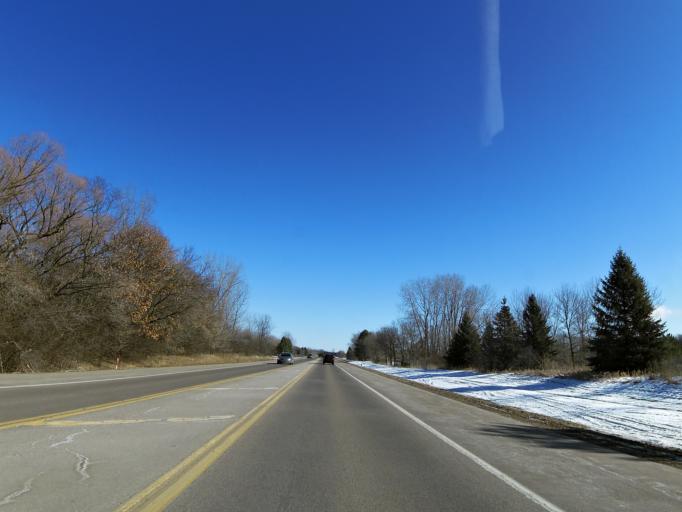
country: US
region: Minnesota
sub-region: Washington County
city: Stillwater
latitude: 45.0577
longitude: -92.8568
